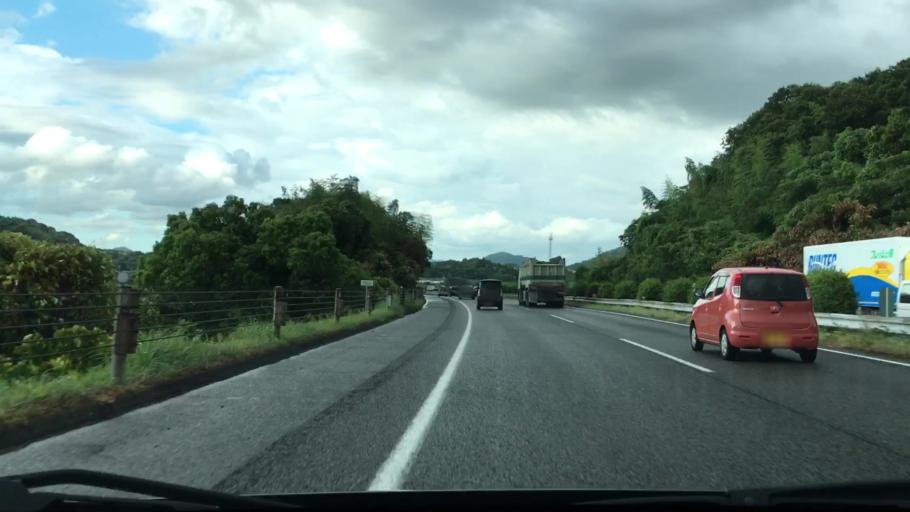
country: JP
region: Fukuoka
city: Koga
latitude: 33.7257
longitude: 130.5029
